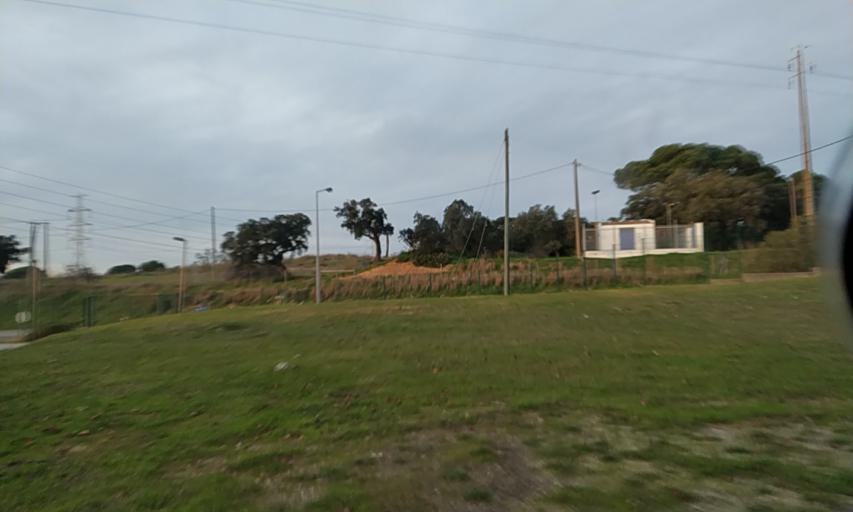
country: PT
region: Setubal
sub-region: Setubal
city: Setubal
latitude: 38.5235
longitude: -8.8414
